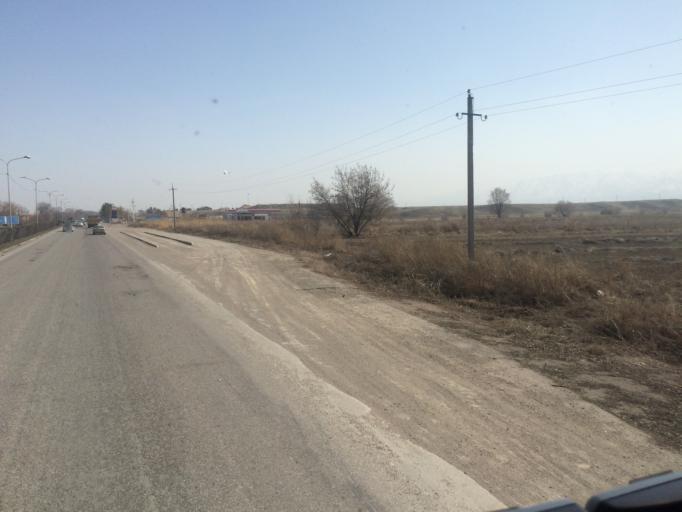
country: KZ
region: Almaty Oblysy
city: Burunday
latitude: 43.2225
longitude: 76.4212
